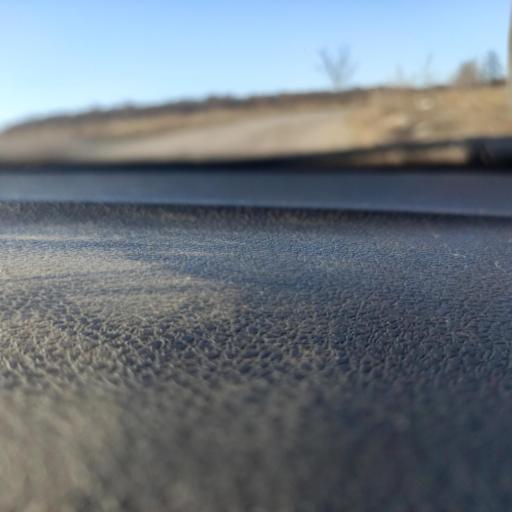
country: RU
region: Bashkortostan
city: Blagoveshchensk
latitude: 54.9105
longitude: 56.0991
